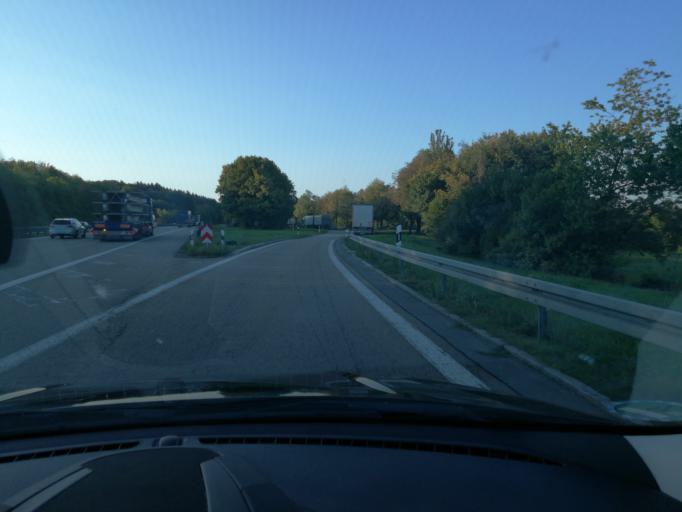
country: DE
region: Bavaria
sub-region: Upper Palatinate
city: Velburg
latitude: 49.2543
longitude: 11.6119
